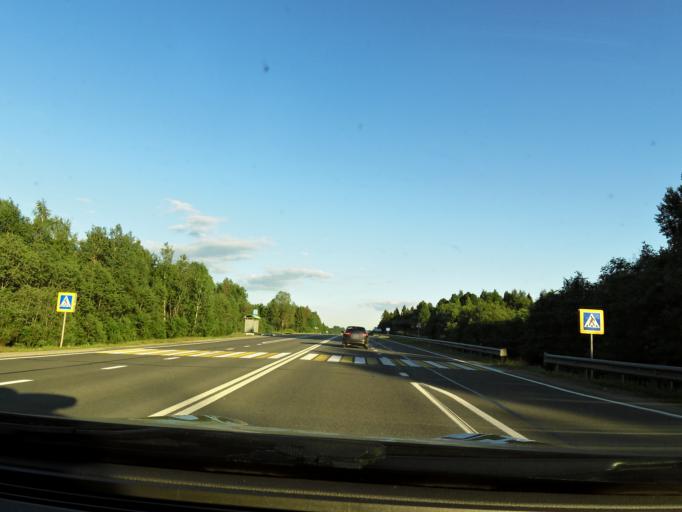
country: RU
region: Vologda
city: Vologda
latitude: 59.1250
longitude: 39.9652
